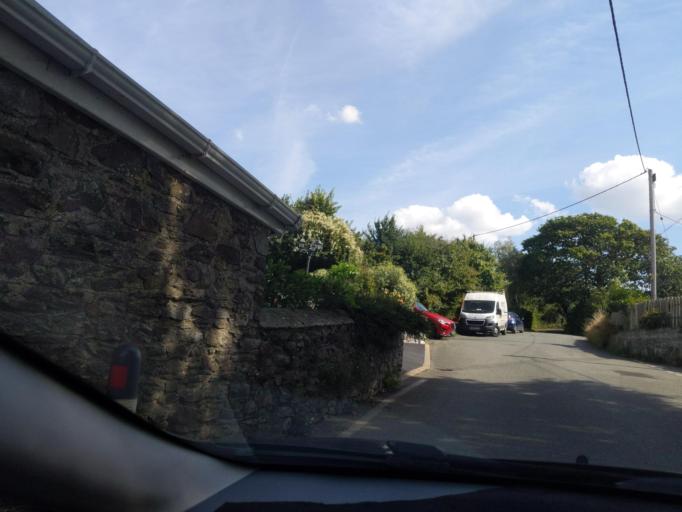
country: GB
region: England
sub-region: Cornwall
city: Torpoint
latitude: 50.3603
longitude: -4.2370
